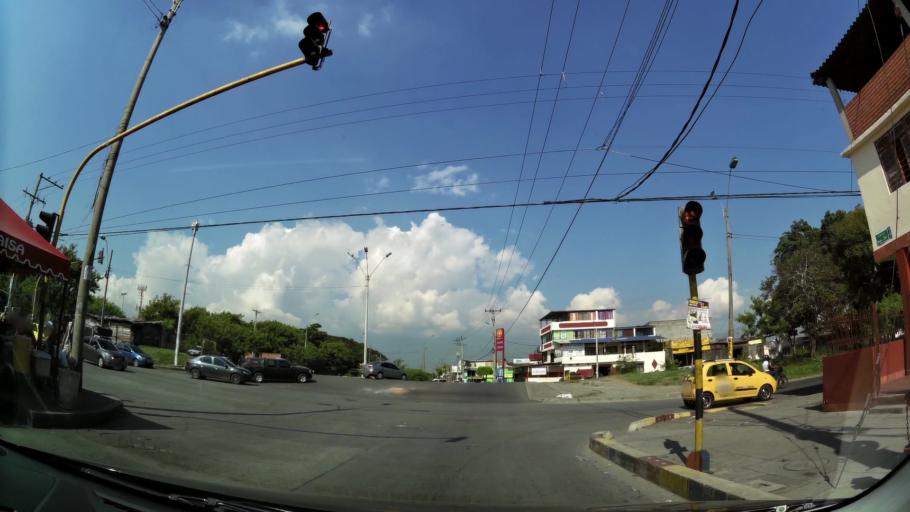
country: CO
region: Valle del Cauca
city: Cali
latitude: 3.4194
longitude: -76.5209
